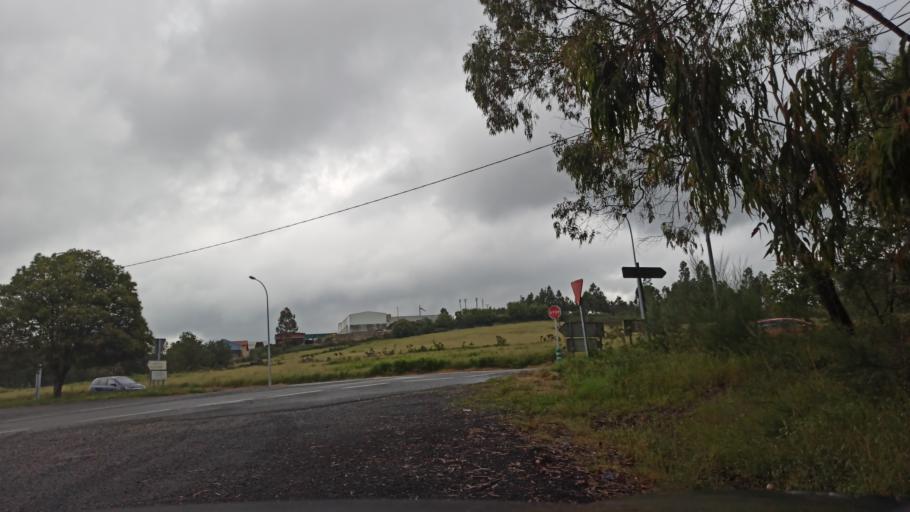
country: ES
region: Galicia
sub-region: Provincia da Coruna
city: Santiso
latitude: 42.7685
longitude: -8.0246
